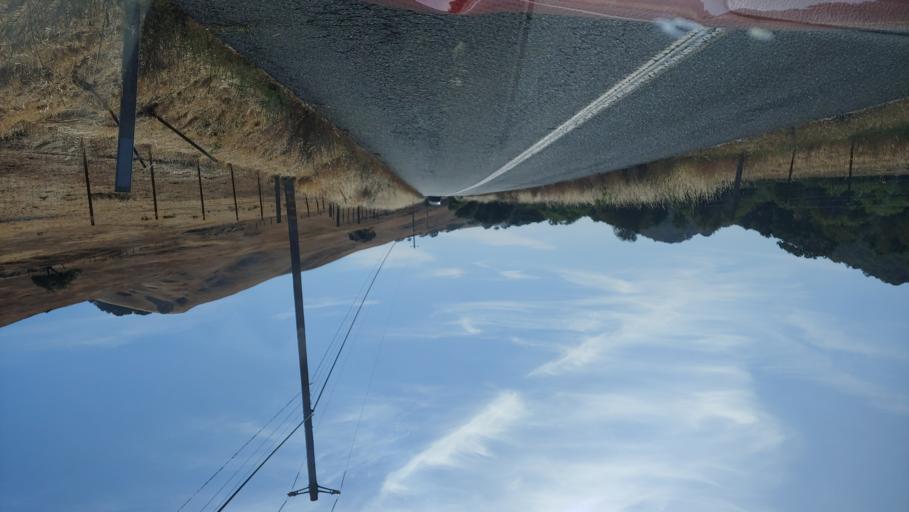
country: US
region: California
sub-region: Sonoma County
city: Petaluma
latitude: 38.1823
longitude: -122.6115
